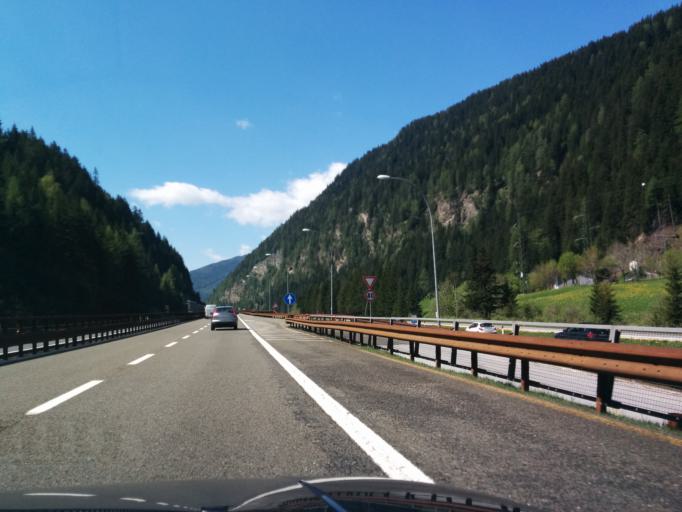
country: IT
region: Trentino-Alto Adige
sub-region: Bolzano
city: Colle Isarco
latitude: 46.9720
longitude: 11.4747
